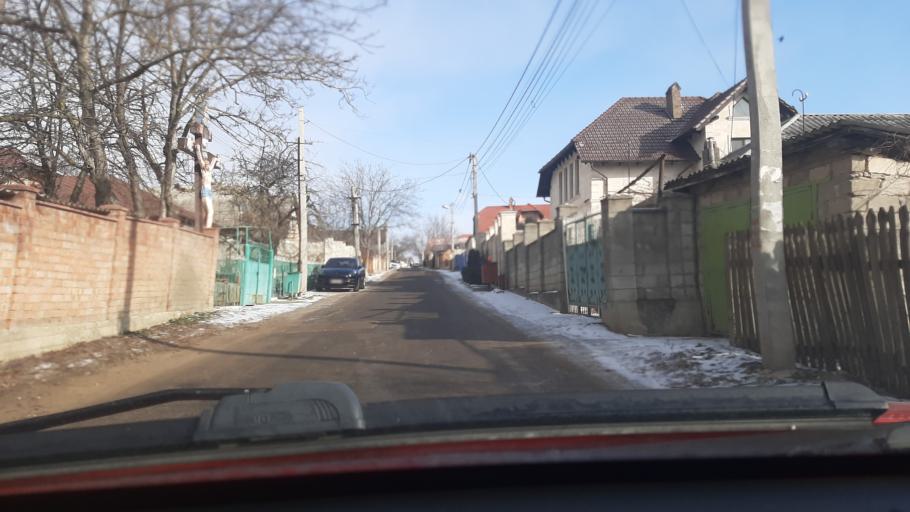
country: MD
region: Laloveni
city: Ialoveni
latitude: 46.9930
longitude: 28.7823
